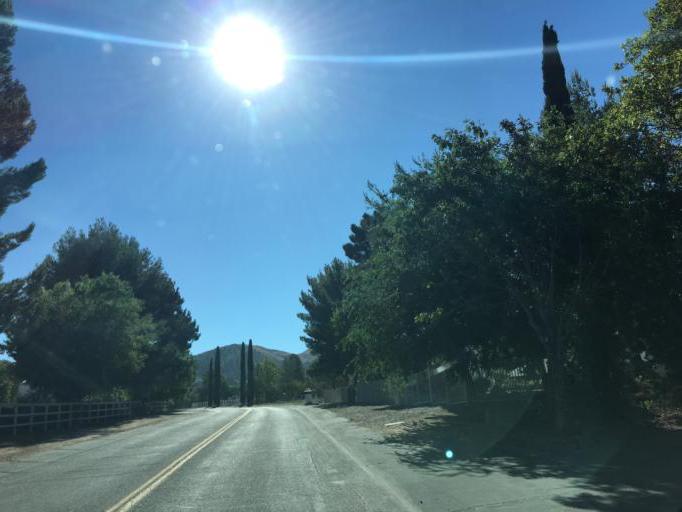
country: US
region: California
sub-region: Los Angeles County
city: Acton
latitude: 34.4576
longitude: -118.1895
